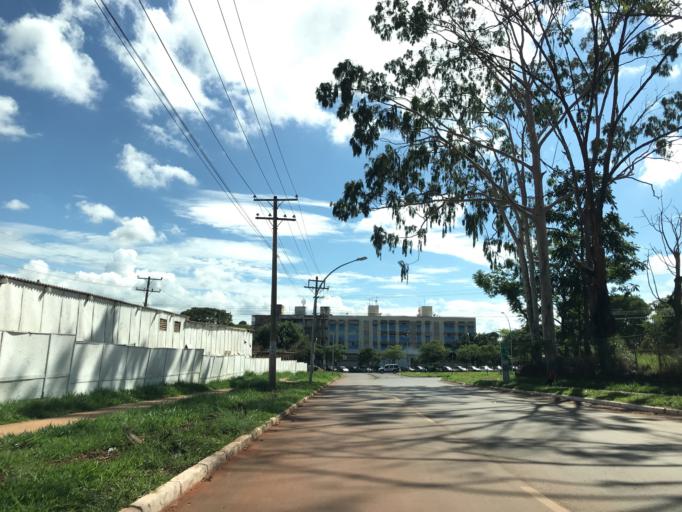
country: BR
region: Federal District
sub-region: Brasilia
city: Brasilia
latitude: -15.7582
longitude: -47.8970
